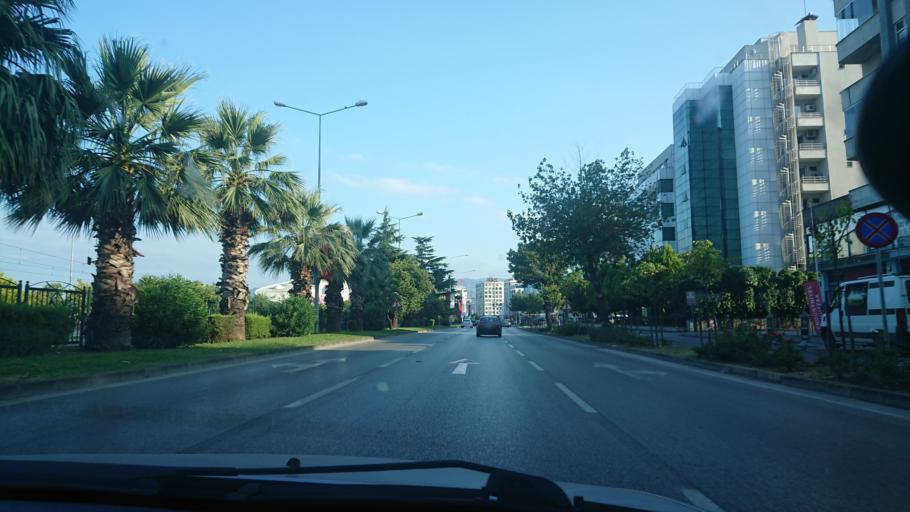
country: TR
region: Samsun
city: Samsun
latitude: 41.2978
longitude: 36.3325
